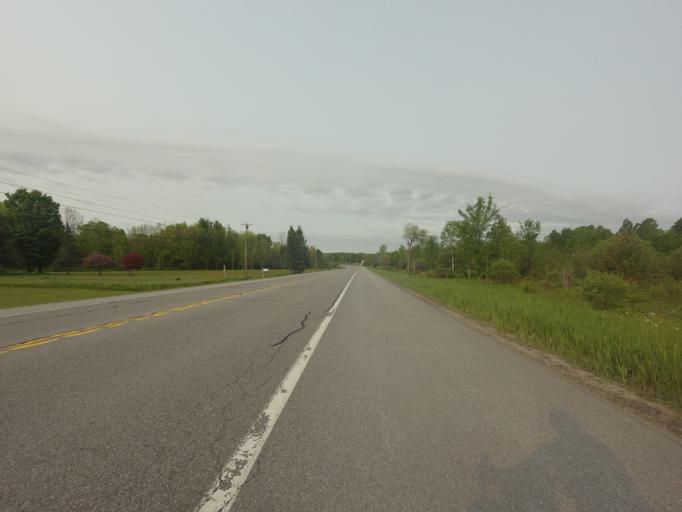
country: US
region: New York
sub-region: Jefferson County
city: Carthage
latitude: 44.0367
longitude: -75.5760
